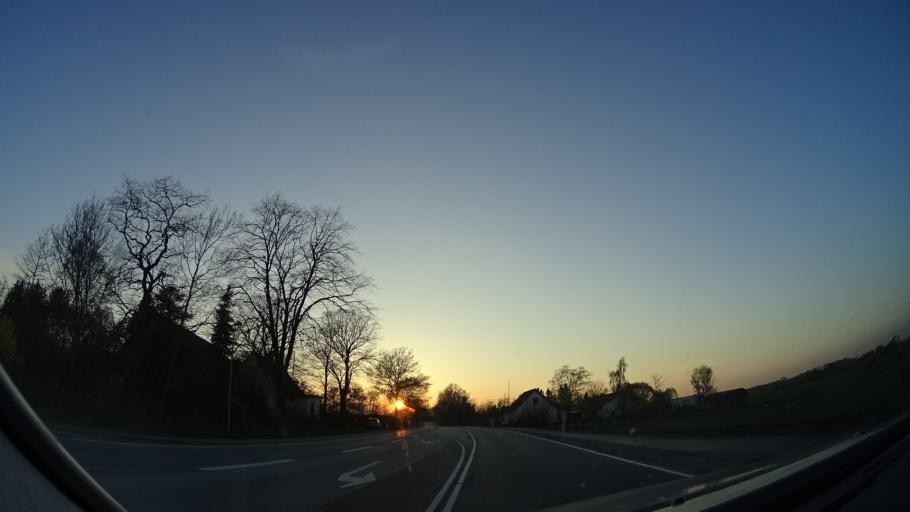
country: DK
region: Zealand
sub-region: Solrod Kommune
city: Solrod
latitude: 55.5534
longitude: 12.1593
